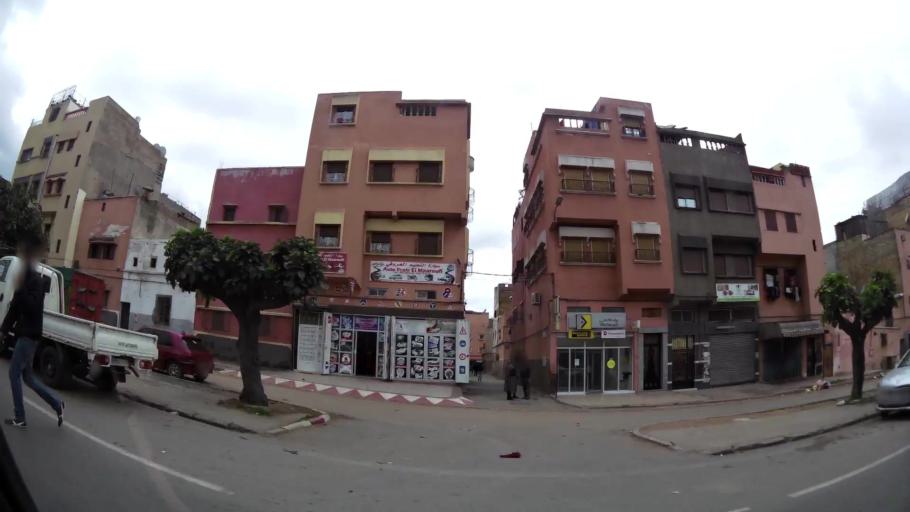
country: MA
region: Grand Casablanca
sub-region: Mediouna
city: Tit Mellil
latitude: 33.5587
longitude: -7.5501
